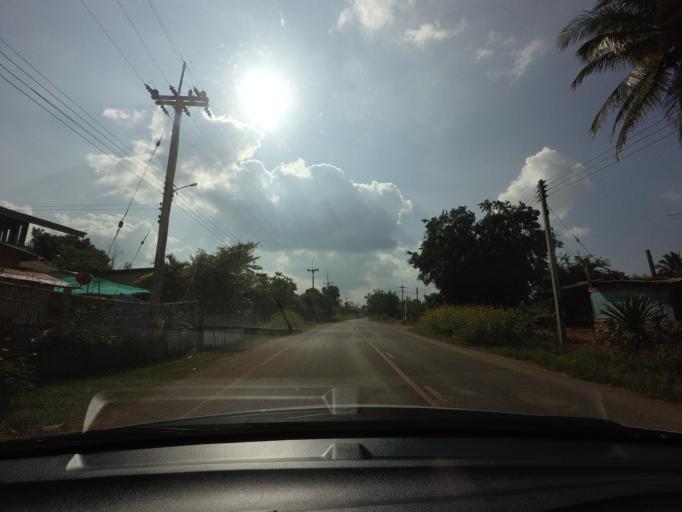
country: TH
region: Nakhon Ratchasima
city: Pak Chong
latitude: 14.5527
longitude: 101.6056
